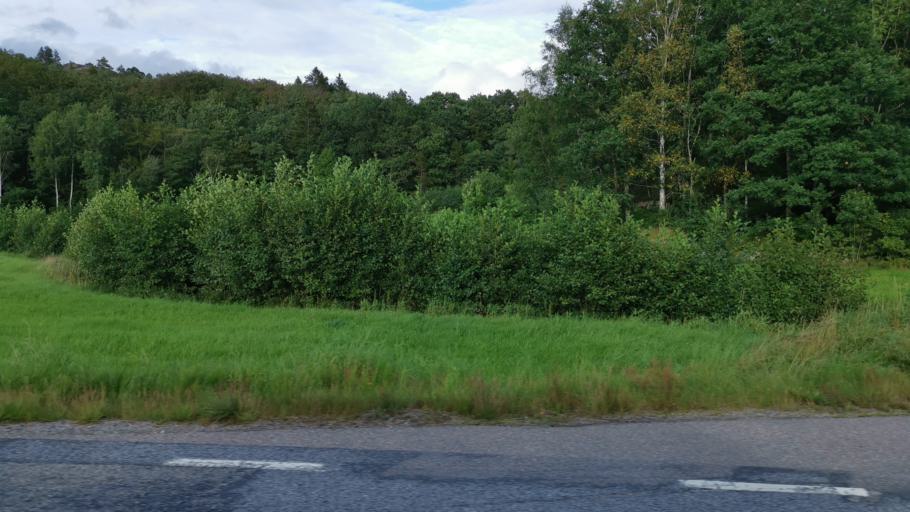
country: SE
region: Vaestra Goetaland
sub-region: Sotenas Kommun
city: Hunnebostrand
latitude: 58.4795
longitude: 11.3982
